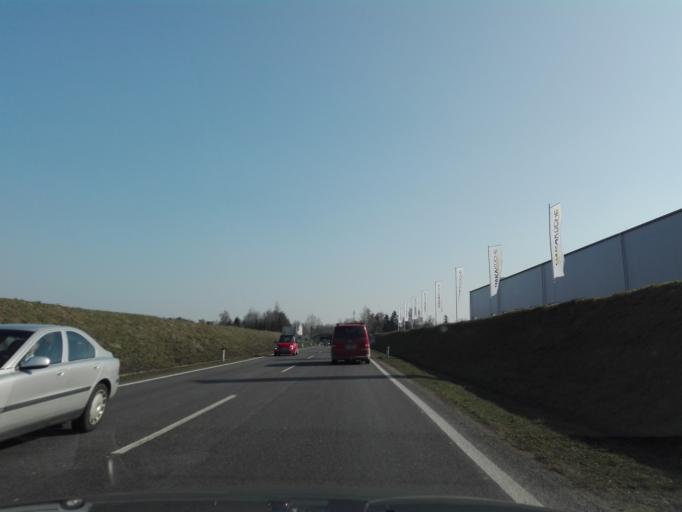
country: AT
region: Upper Austria
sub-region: Politischer Bezirk Linz-Land
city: Traun
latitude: 48.2222
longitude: 14.2266
